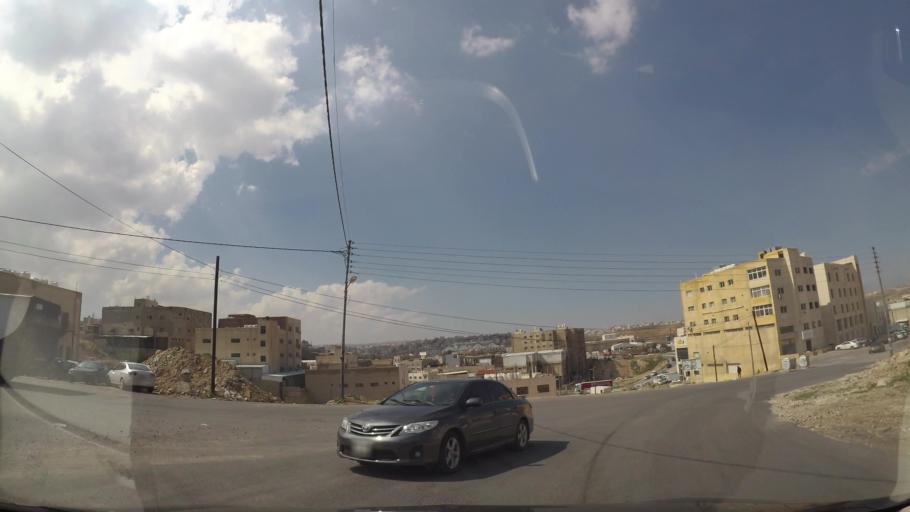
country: JO
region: Zarqa
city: Russeifa
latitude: 31.9934
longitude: 35.9957
